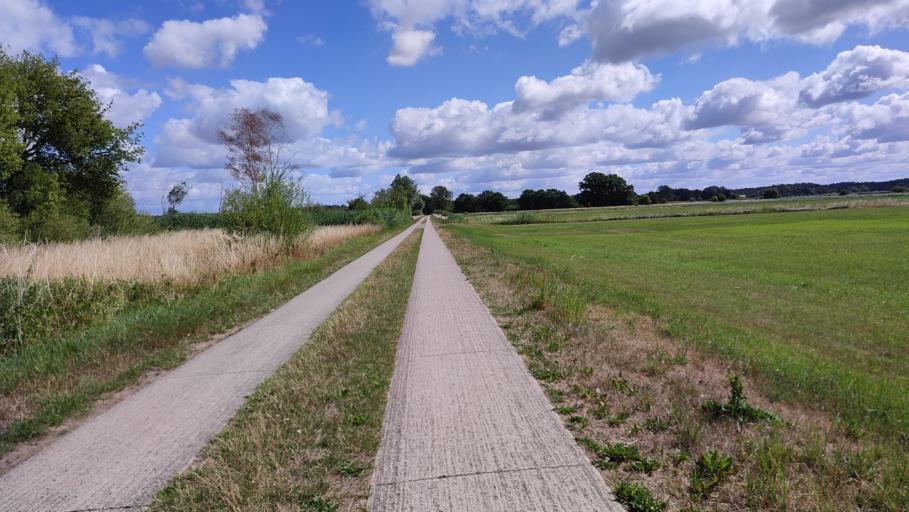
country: DE
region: Lower Saxony
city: Neu Darchau
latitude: 53.2207
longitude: 10.9725
